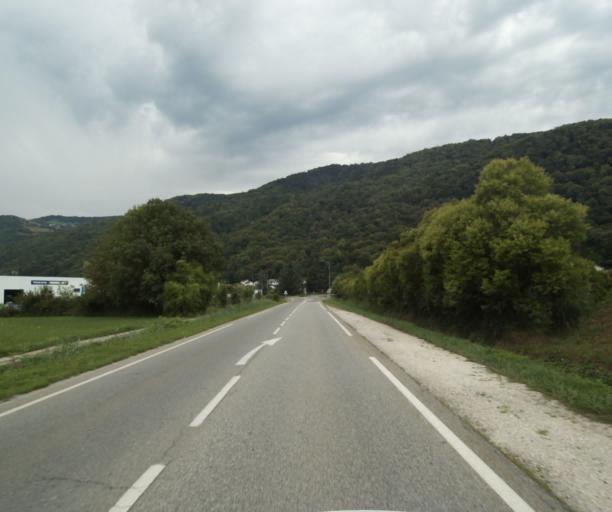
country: FR
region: Rhone-Alpes
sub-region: Departement de l'Isere
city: Domene
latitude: 45.2079
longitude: 5.8462
